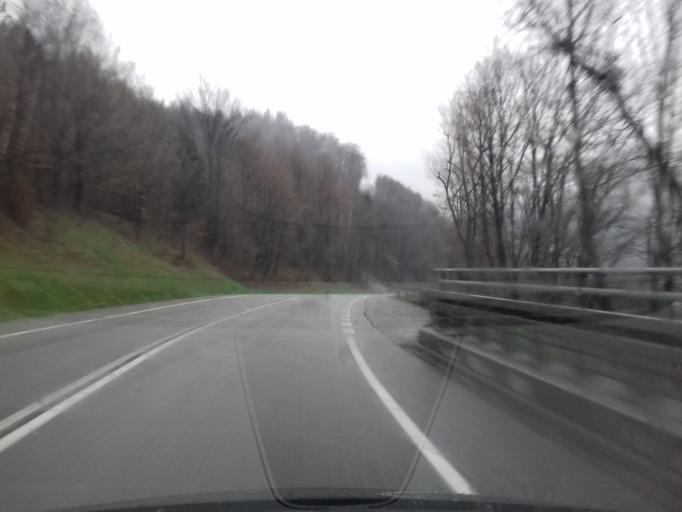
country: PL
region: Lesser Poland Voivodeship
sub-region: Powiat nowosadecki
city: Piwniczna-Zdroj
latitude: 49.4581
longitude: 20.6939
